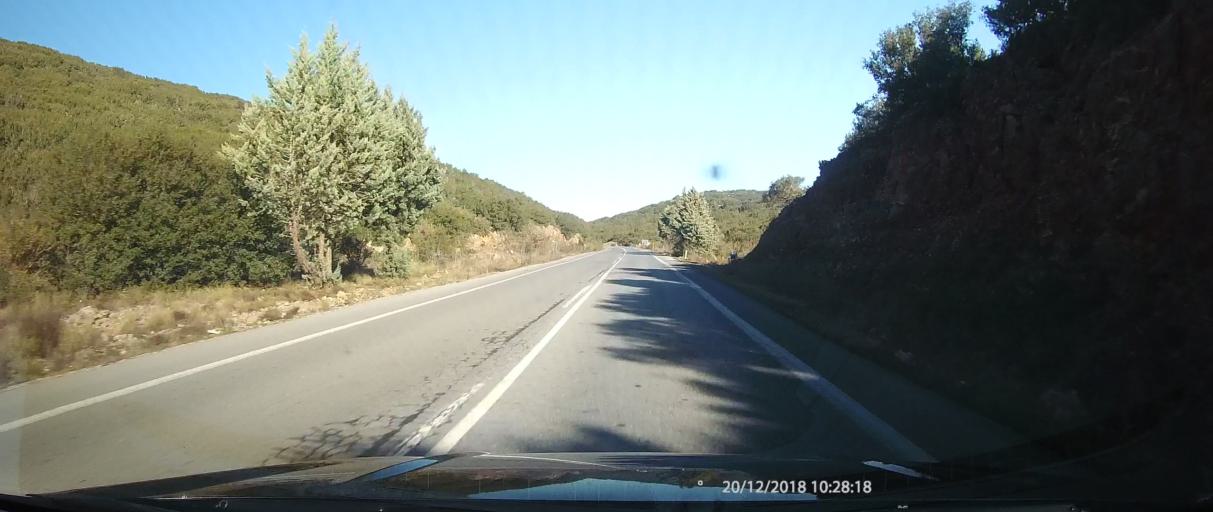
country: GR
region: Peloponnese
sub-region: Nomos Lakonias
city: Kariai
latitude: 37.2597
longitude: 22.4362
